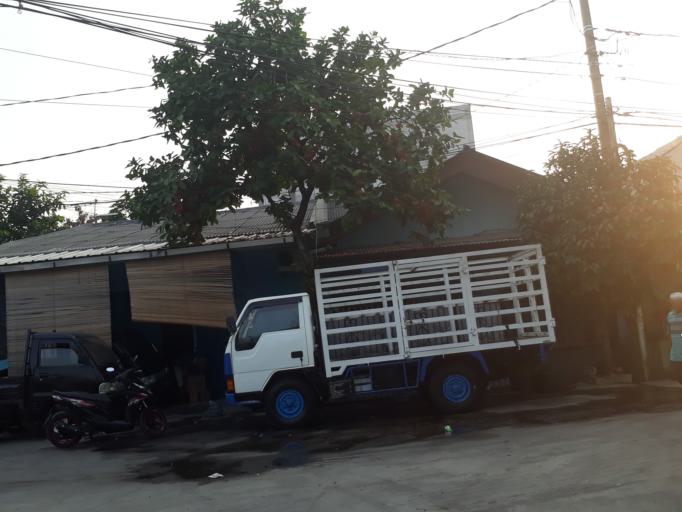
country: ID
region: West Java
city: Bekasi
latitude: -6.2450
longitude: 107.0529
